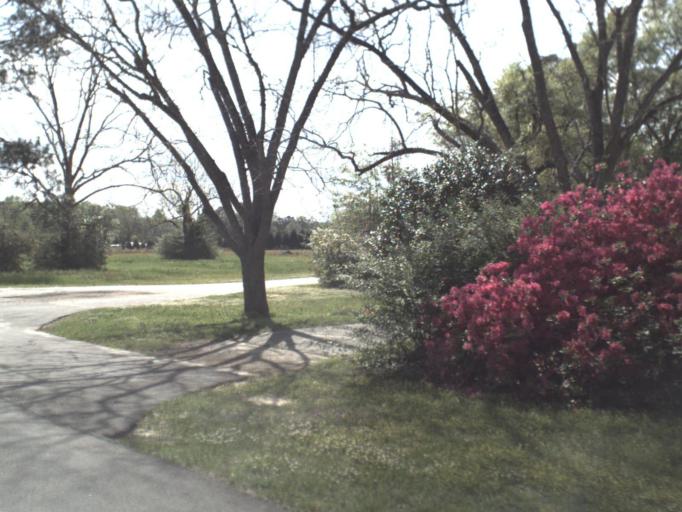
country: US
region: Alabama
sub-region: Covington County
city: Florala
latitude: 30.9603
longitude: -86.4661
